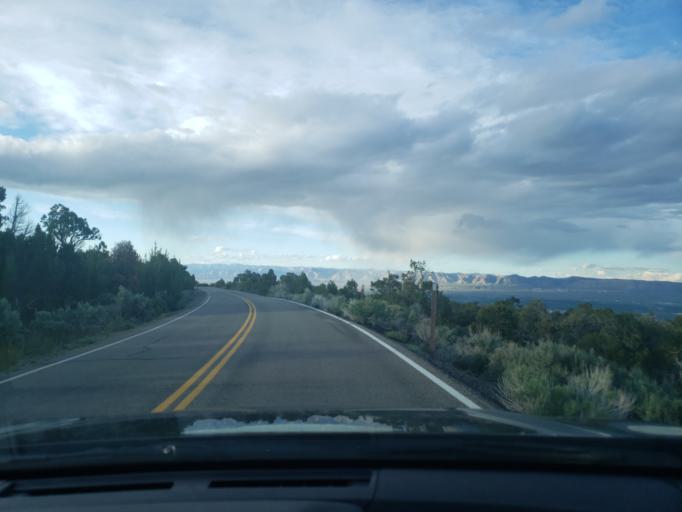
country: US
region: Colorado
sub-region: Mesa County
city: Redlands
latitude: 39.0298
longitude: -108.6602
